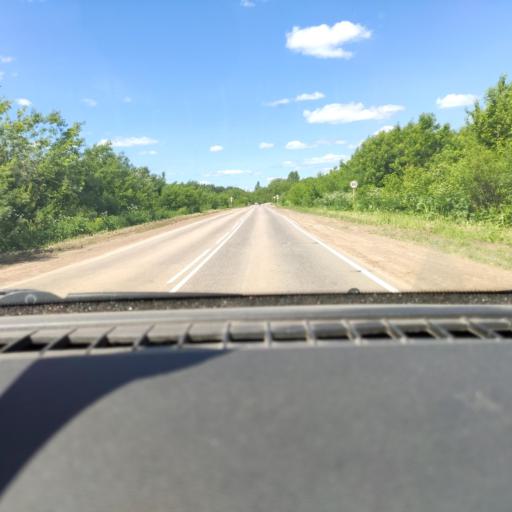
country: RU
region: Perm
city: Chaykovskaya
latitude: 58.1092
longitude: 55.5872
